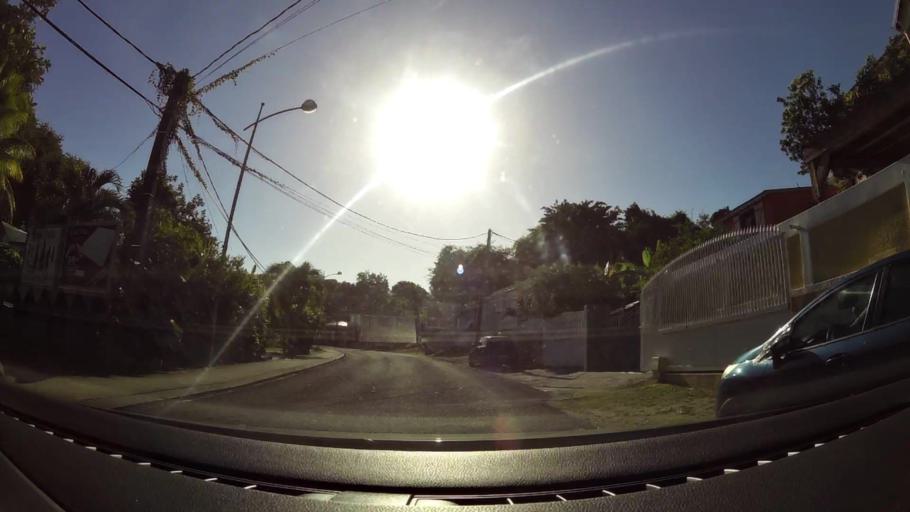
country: GP
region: Guadeloupe
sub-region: Guadeloupe
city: Le Gosier
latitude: 16.2099
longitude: -61.4807
